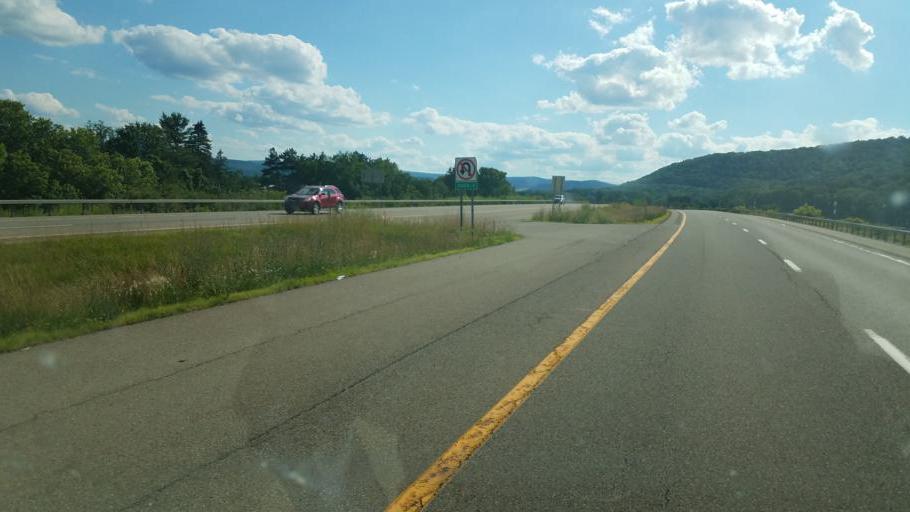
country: US
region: New York
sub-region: Cattaraugus County
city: Olean
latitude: 42.0990
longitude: -78.4359
